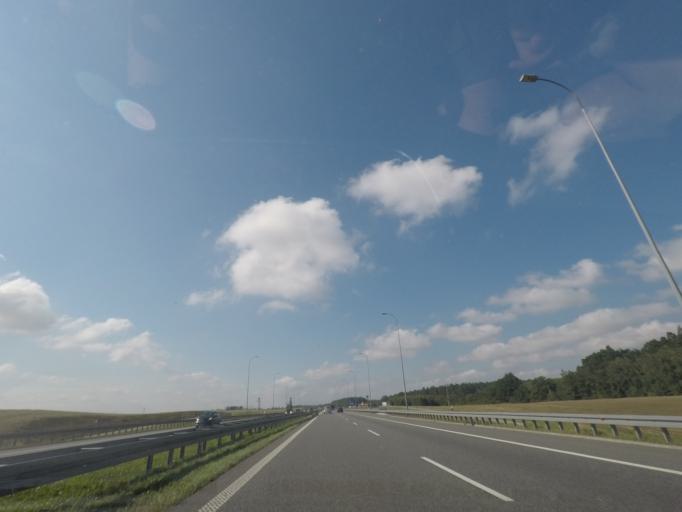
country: PL
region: Pomeranian Voivodeship
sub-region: Powiat tczewski
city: Pelplin
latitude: 53.8936
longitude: 18.6348
